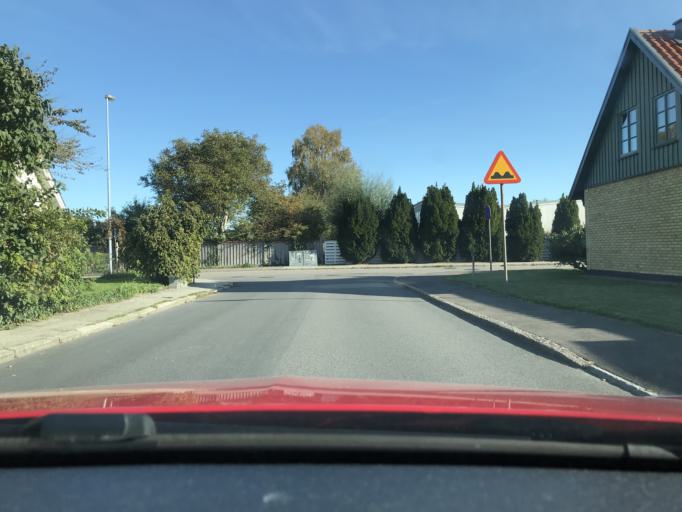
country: SE
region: Skane
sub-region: Lunds Kommun
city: Lund
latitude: 55.6931
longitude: 13.2042
